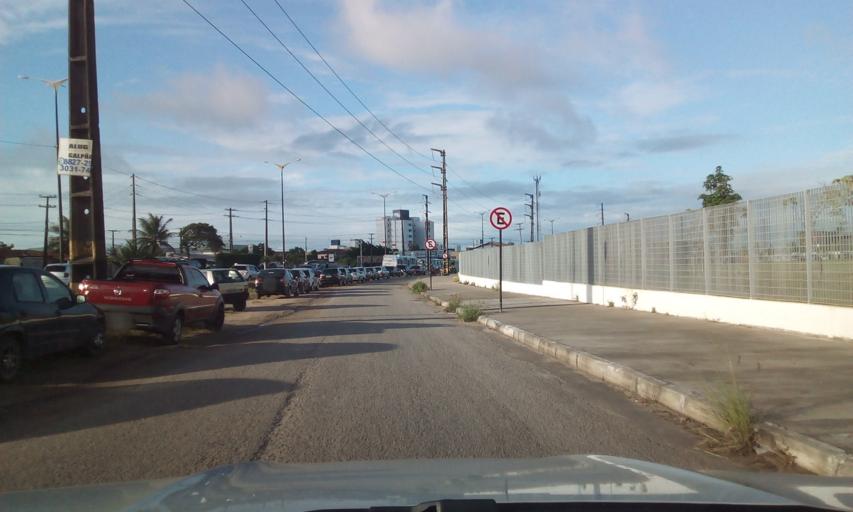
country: BR
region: Paraiba
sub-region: Joao Pessoa
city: Joao Pessoa
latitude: -7.1615
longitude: -34.8224
